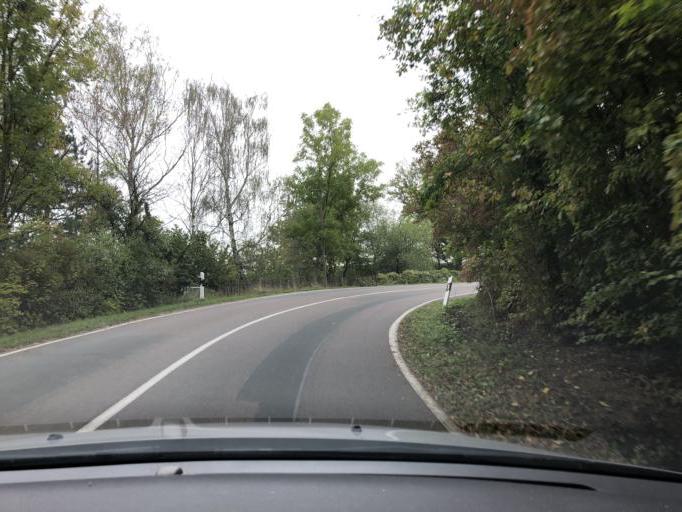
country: DE
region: Saxony-Anhalt
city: Bad Kosen
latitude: 51.1550
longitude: 11.7550
